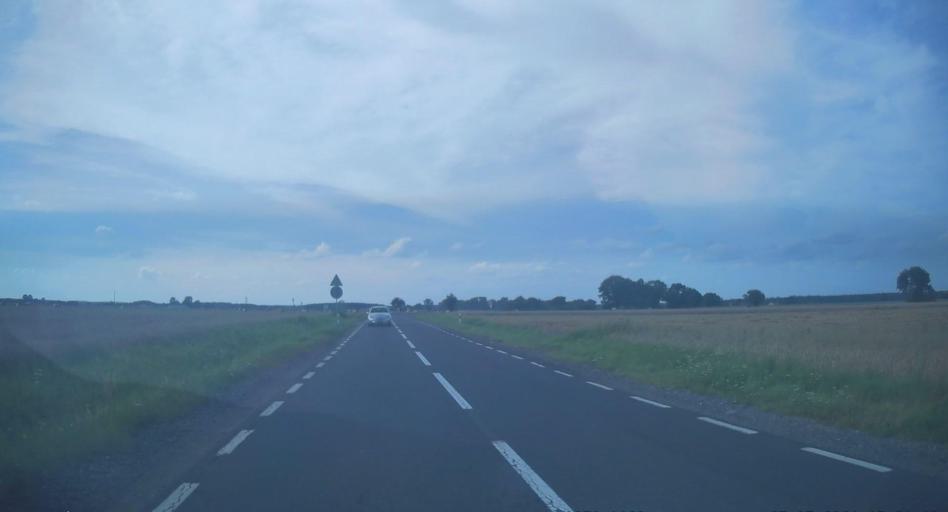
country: PL
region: Lodz Voivodeship
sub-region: Powiat tomaszowski
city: Rzeczyca
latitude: 51.6670
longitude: 20.2643
